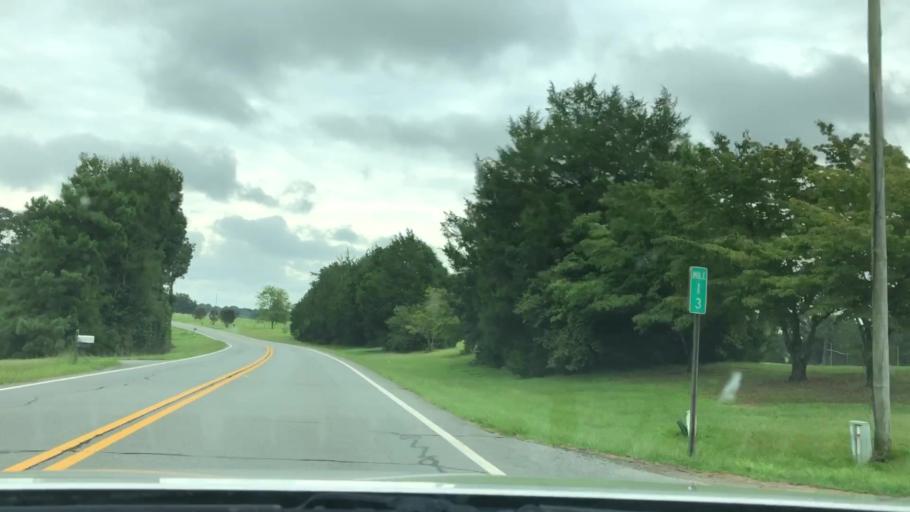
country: US
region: Georgia
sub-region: Pike County
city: Zebulon
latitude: 33.1093
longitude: -84.3887
